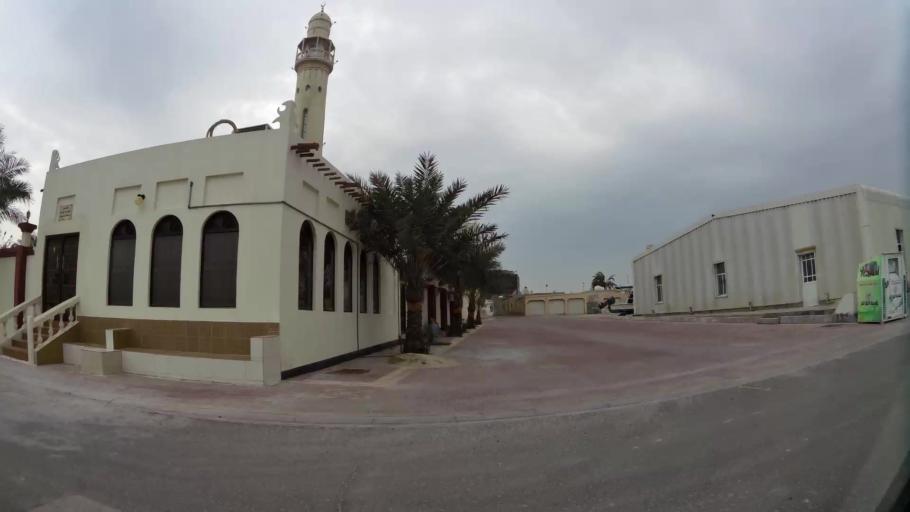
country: BH
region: Northern
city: Ar Rifa'
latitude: 26.0558
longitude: 50.6196
